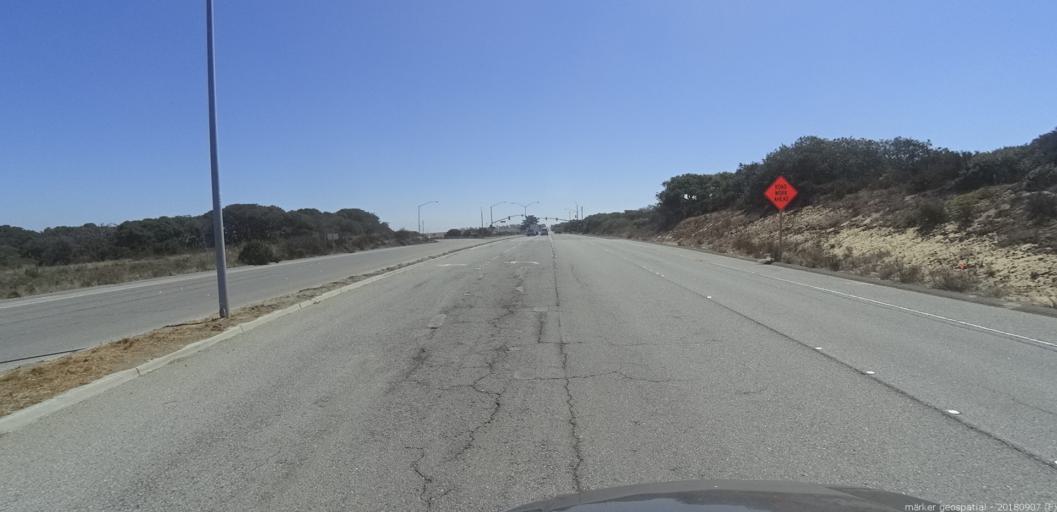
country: US
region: California
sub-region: Monterey County
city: Marina
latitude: 36.6678
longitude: -121.7588
